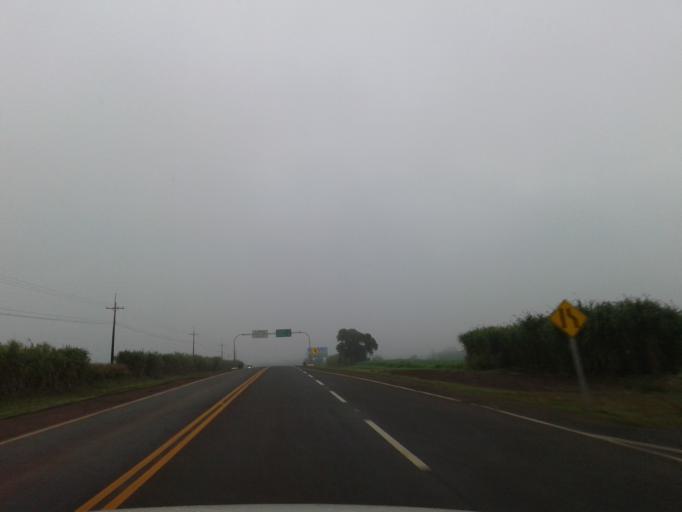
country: PY
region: Itapua
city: Pirapo
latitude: -26.9023
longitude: -55.4765
